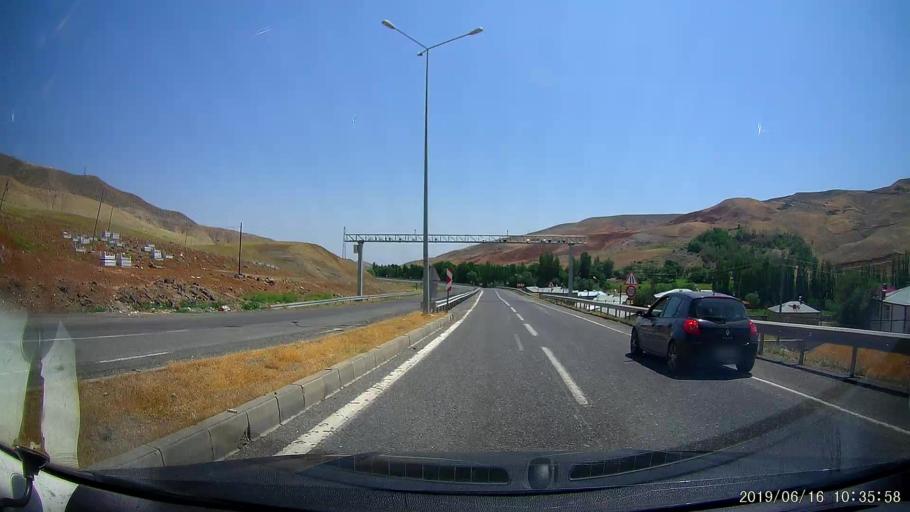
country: TR
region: Igdir
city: Tuzluca
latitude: 40.0362
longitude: 43.6761
